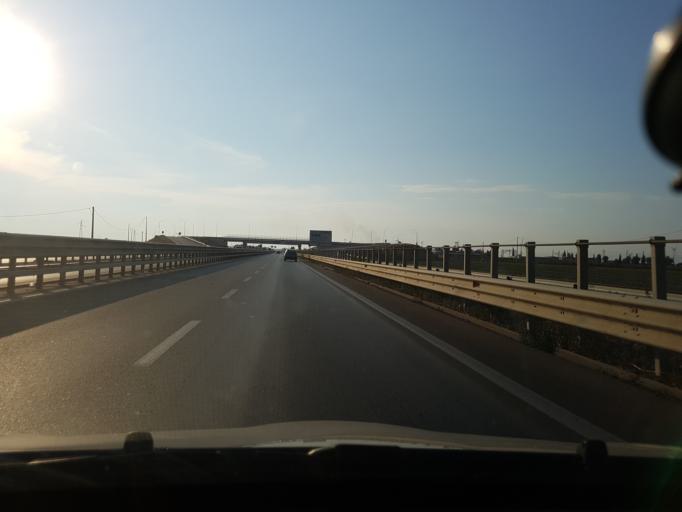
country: IT
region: Apulia
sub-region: Provincia di Foggia
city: Orta Nova
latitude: 41.3433
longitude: 15.7408
